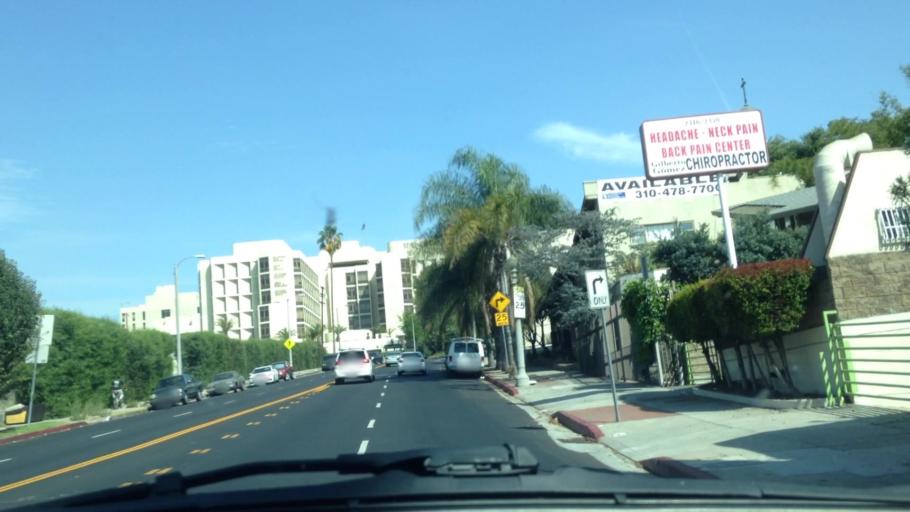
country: US
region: California
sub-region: Los Angeles County
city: Echo Park
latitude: 34.0647
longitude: -118.2762
